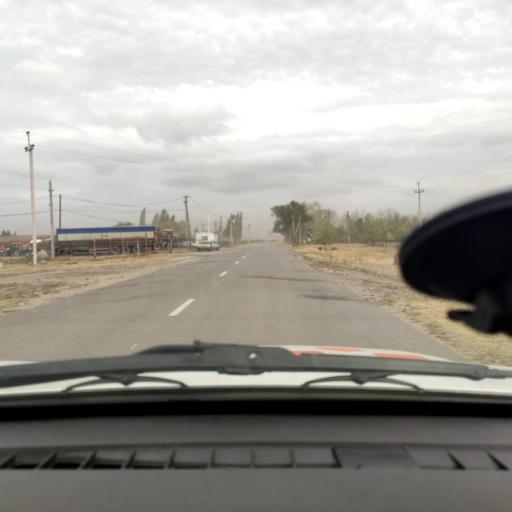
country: RU
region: Lipetsk
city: Khlevnoye
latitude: 52.0053
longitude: 39.1201
